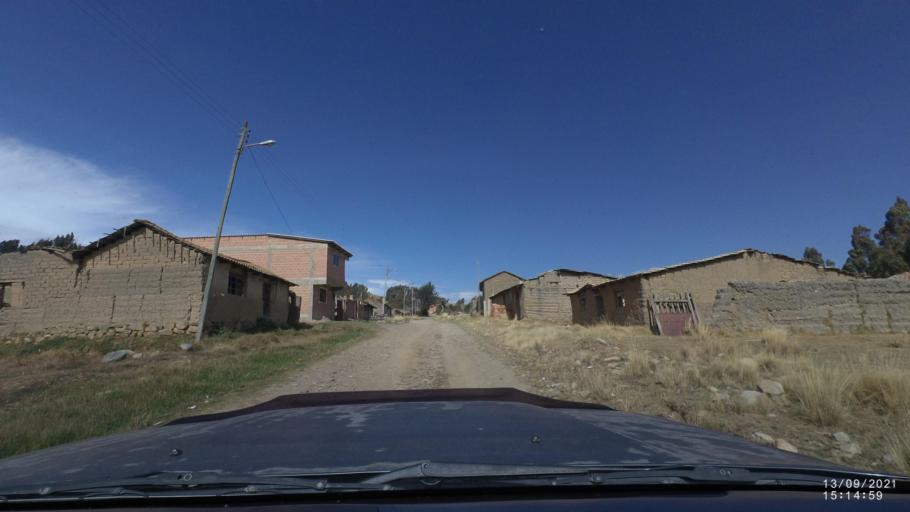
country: BO
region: Cochabamba
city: Colomi
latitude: -17.3672
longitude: -65.7969
